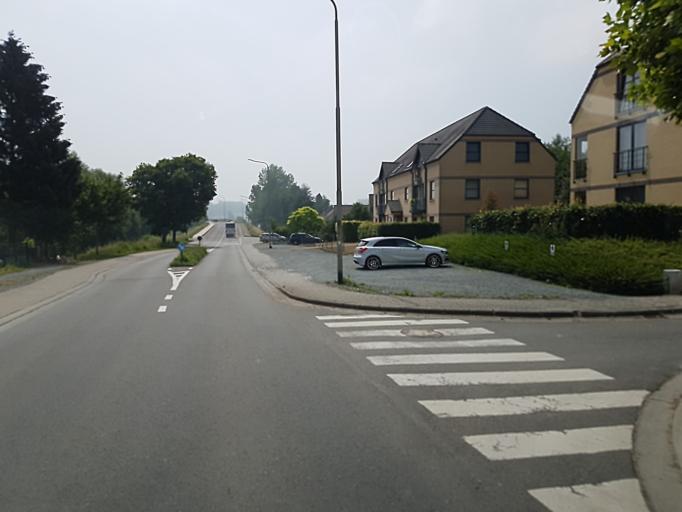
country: BE
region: Flanders
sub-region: Provincie Oost-Vlaanderen
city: Geraardsbergen
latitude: 50.7961
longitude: 3.8997
